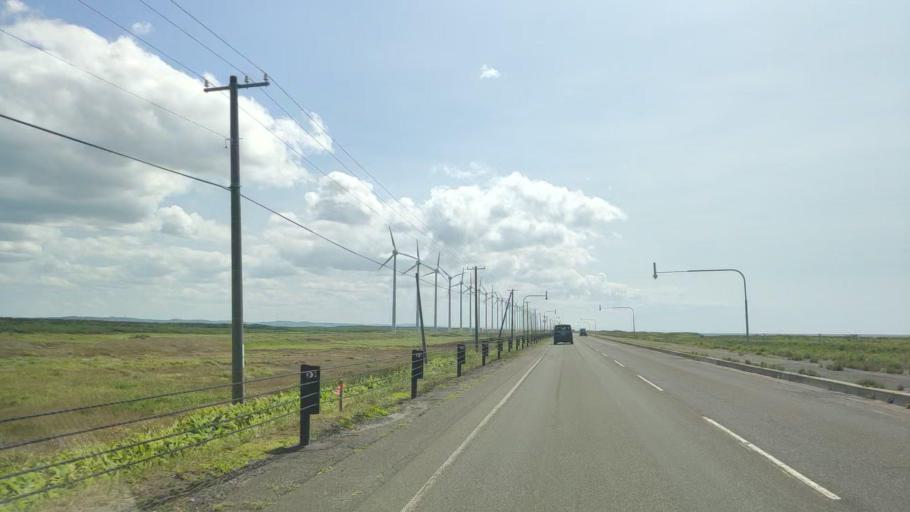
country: JP
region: Hokkaido
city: Makubetsu
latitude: 44.9865
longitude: 141.6901
